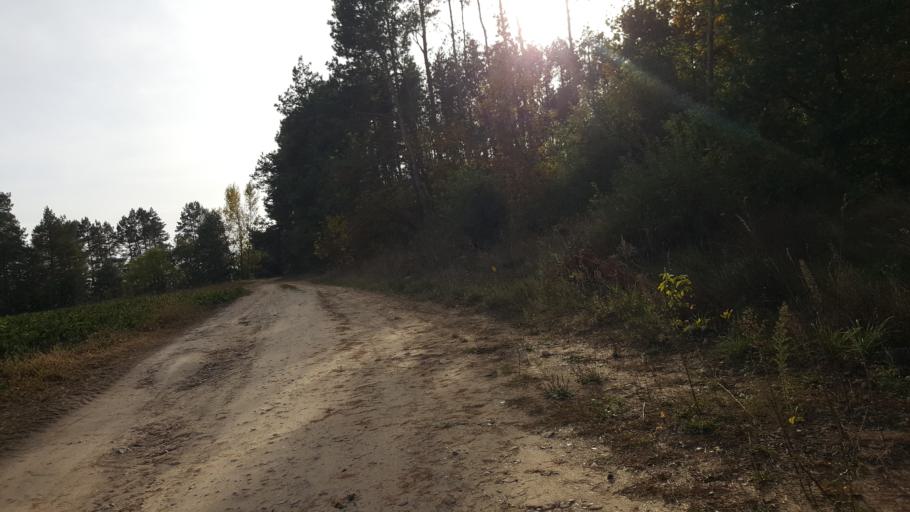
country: BY
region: Brest
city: Kamyanyets
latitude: 52.3883
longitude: 23.8476
